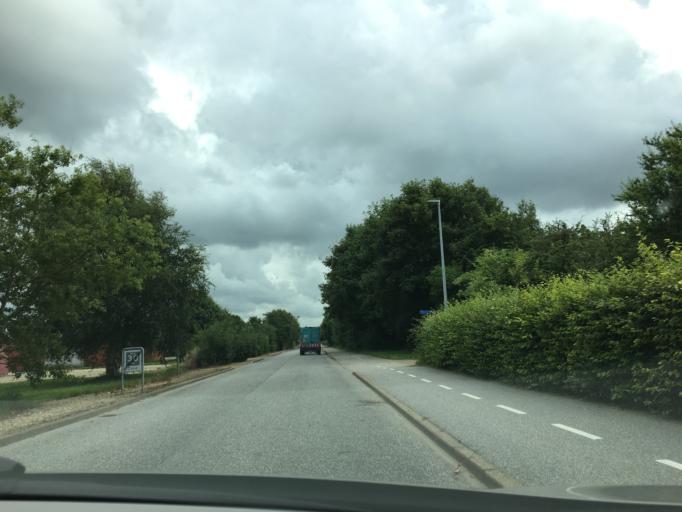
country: DK
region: South Denmark
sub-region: Varde Kommune
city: Oksbol
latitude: 55.7382
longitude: 8.2658
